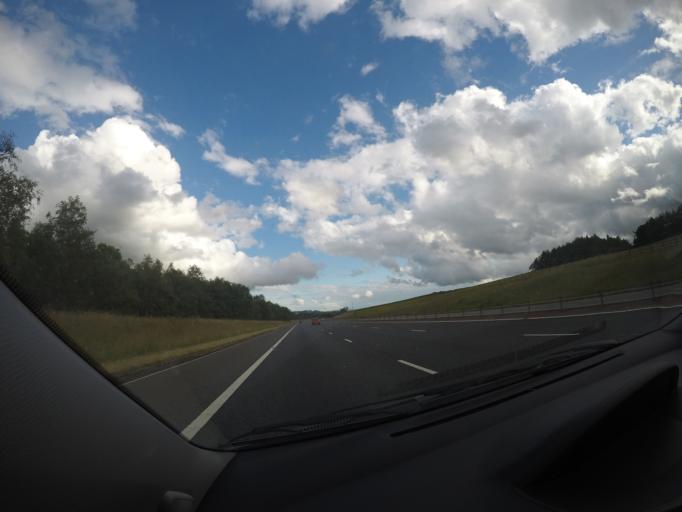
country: GB
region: Scotland
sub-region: Dumfries and Galloway
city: Lockerbie
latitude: 55.1692
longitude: -3.3917
